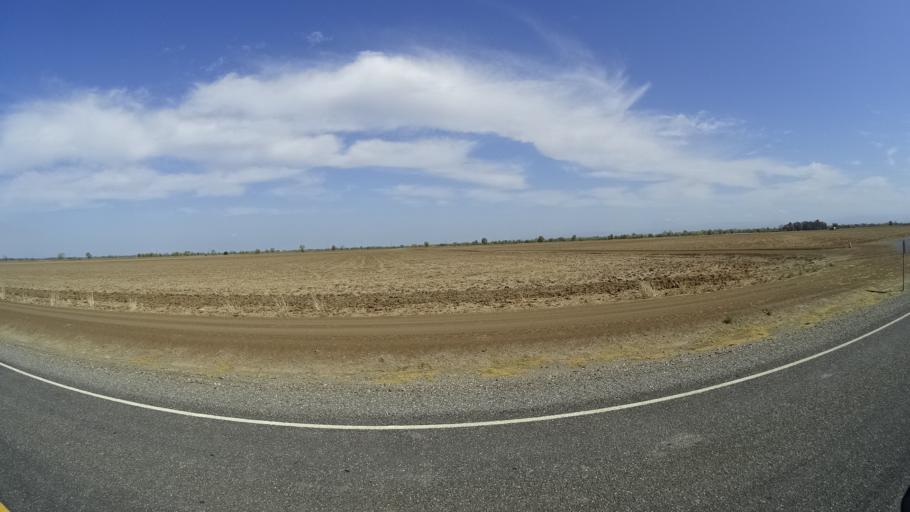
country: US
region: California
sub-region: Butte County
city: Durham
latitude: 39.5364
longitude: -121.9205
